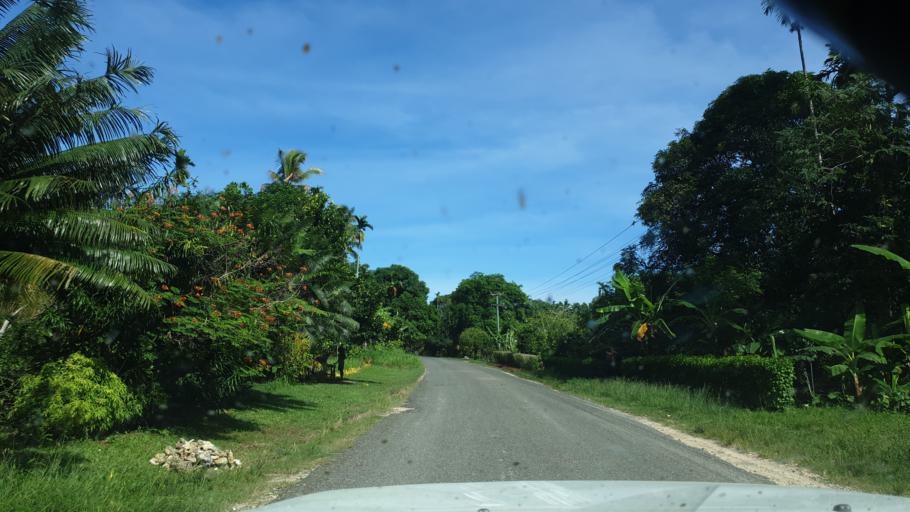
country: PG
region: Madang
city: Madang
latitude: -4.8151
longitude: 145.7668
